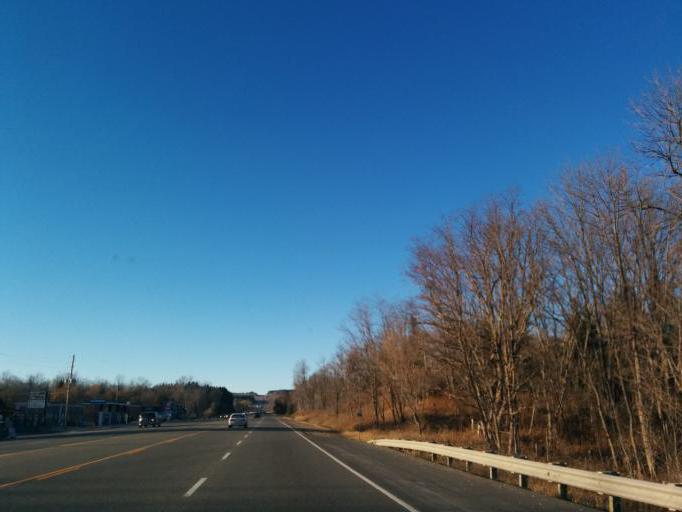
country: CA
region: Ontario
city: Orangeville
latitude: 43.8225
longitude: -79.9446
